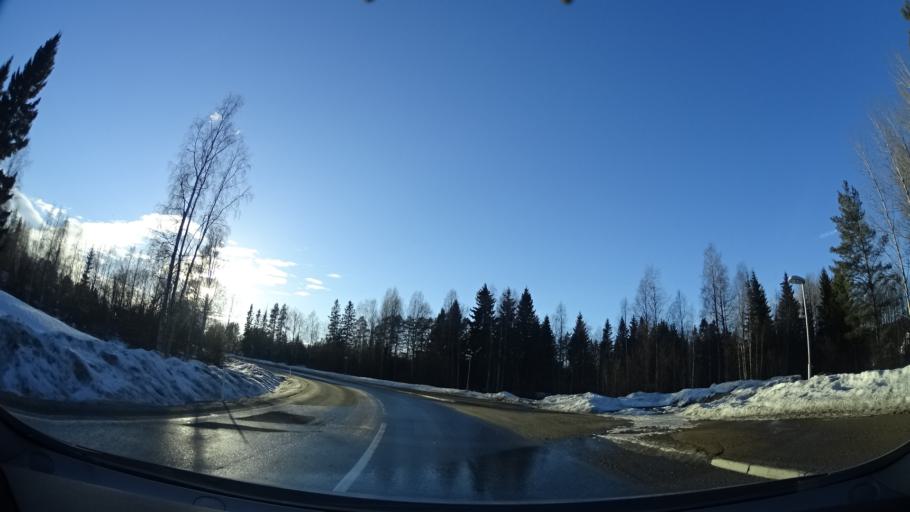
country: SE
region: Vaesterbotten
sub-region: Skelleftea Kommun
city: Byske
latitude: 64.9517
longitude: 21.1916
